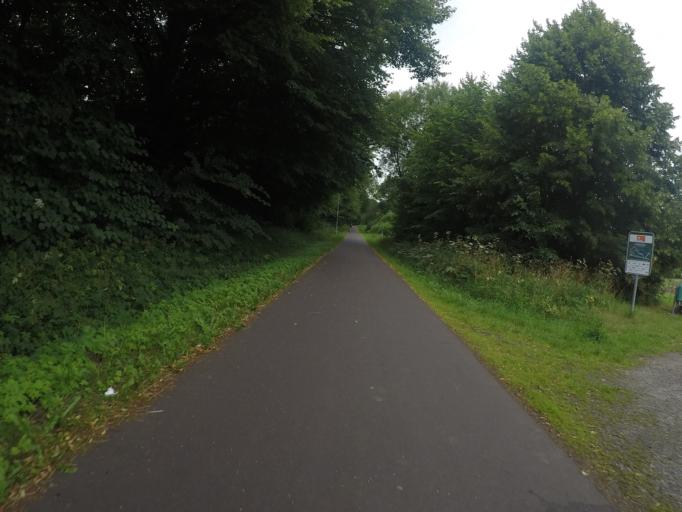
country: DE
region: Lower Saxony
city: Stade
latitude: 53.5983
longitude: 9.4563
